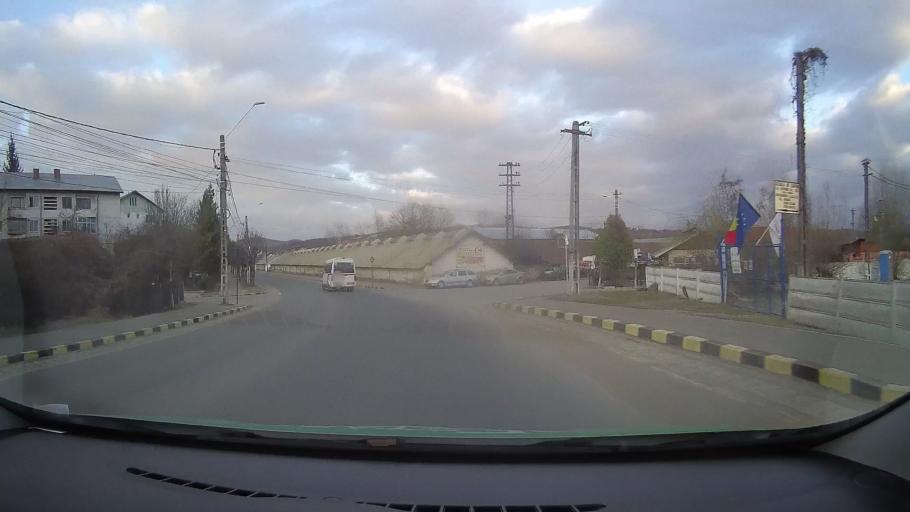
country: RO
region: Dambovita
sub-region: Municipiul Moreni
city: Moreni
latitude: 44.9791
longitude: 25.6369
